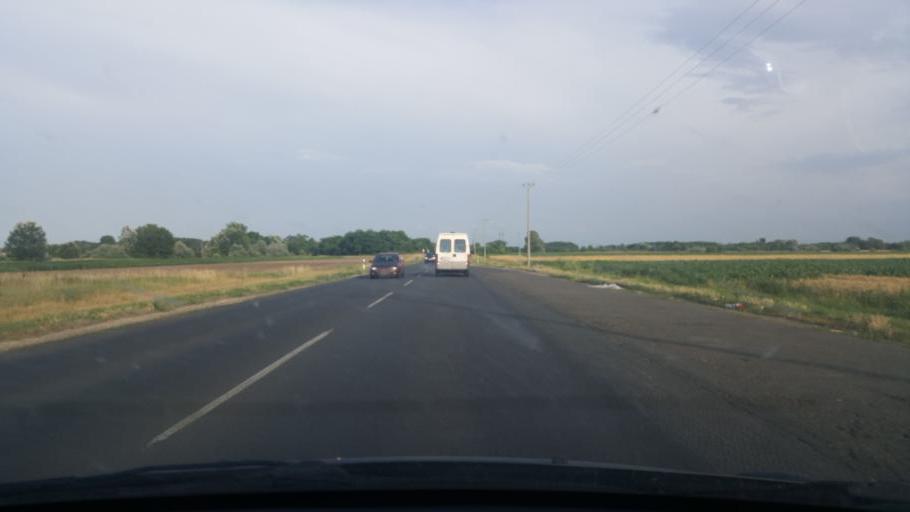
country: HU
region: Pest
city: Ullo
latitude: 47.3671
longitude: 19.3789
